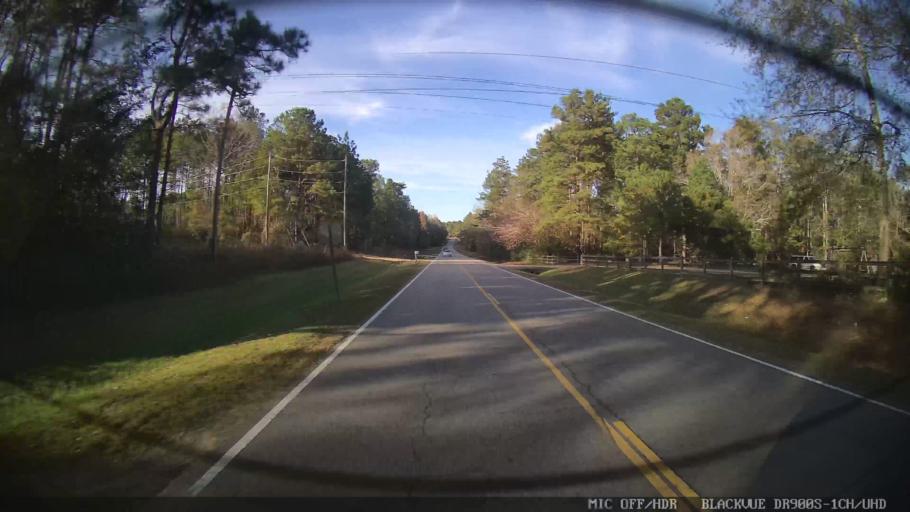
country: US
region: Mississippi
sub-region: Forrest County
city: Hattiesburg
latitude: 31.2041
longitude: -89.2933
